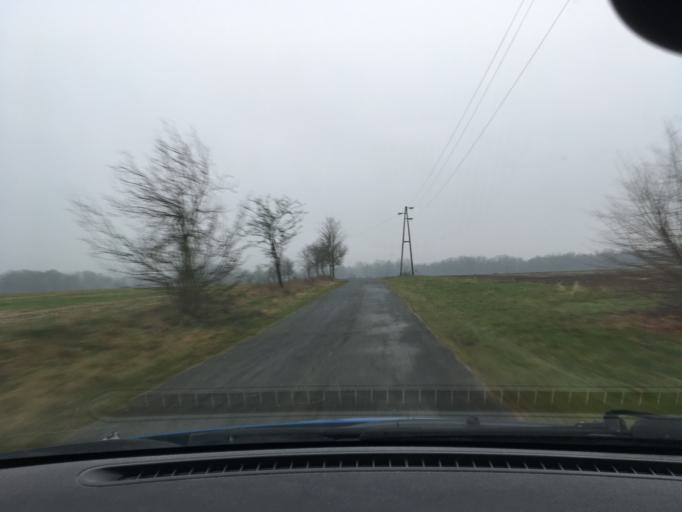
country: DE
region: Lower Saxony
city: Soderstorf
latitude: 53.0939
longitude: 10.1607
